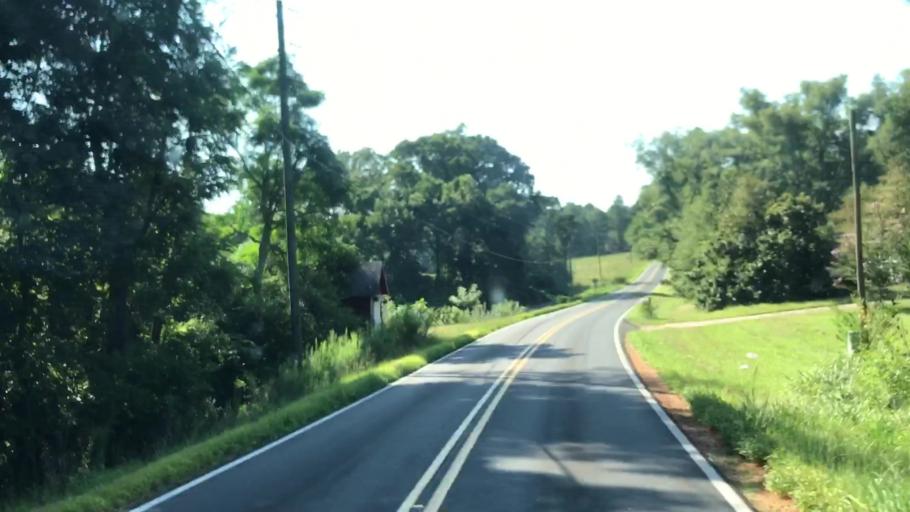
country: US
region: Georgia
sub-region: Walton County
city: Monroe
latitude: 33.8553
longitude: -83.7882
